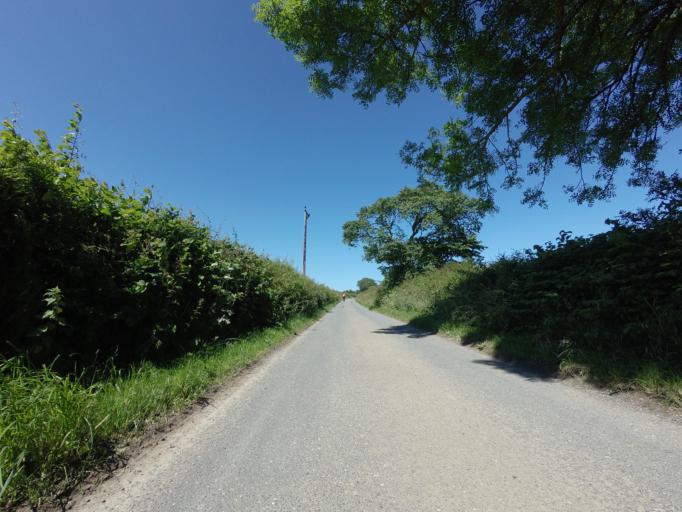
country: GB
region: Scotland
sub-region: Aberdeenshire
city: Macduff
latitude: 57.6339
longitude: -2.4898
